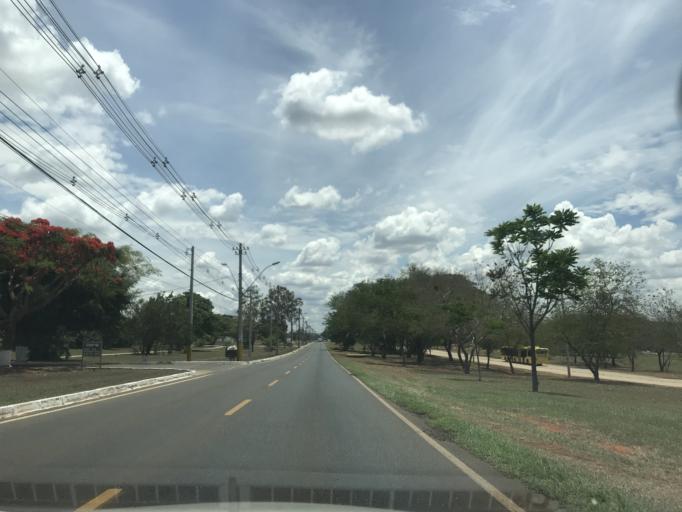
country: BR
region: Federal District
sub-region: Brasilia
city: Brasilia
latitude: -15.8684
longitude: -47.9436
